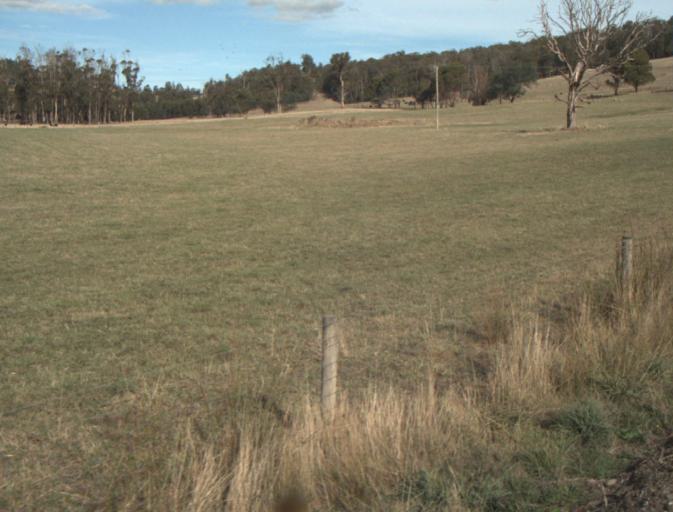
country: AU
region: Tasmania
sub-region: Launceston
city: Mayfield
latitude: -41.2194
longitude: 147.1584
